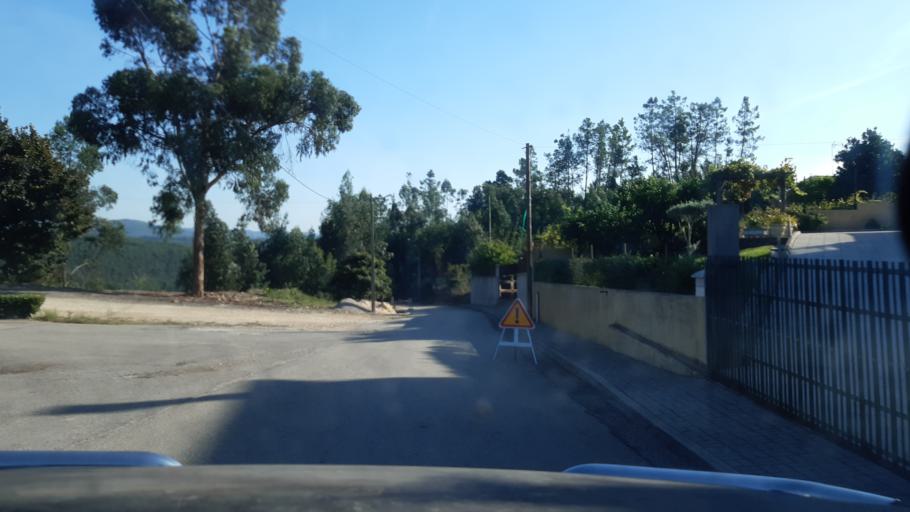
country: PT
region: Aveiro
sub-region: Agueda
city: Aguada de Cima
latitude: 40.5694
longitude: -8.3638
